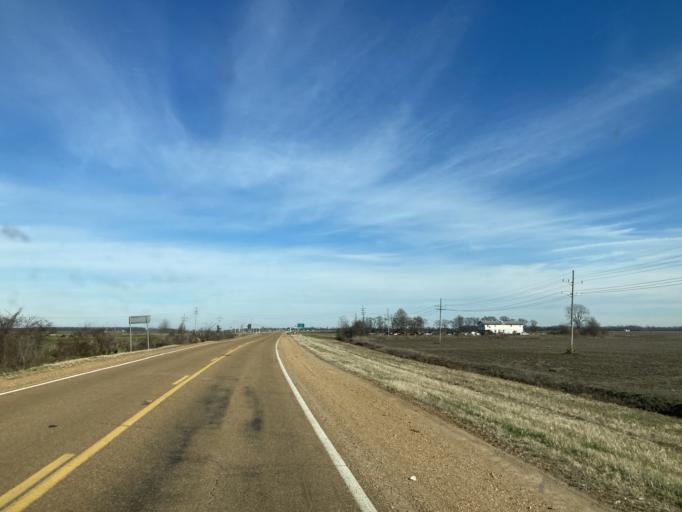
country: US
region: Mississippi
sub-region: Humphreys County
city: Belzoni
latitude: 32.9935
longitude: -90.5887
